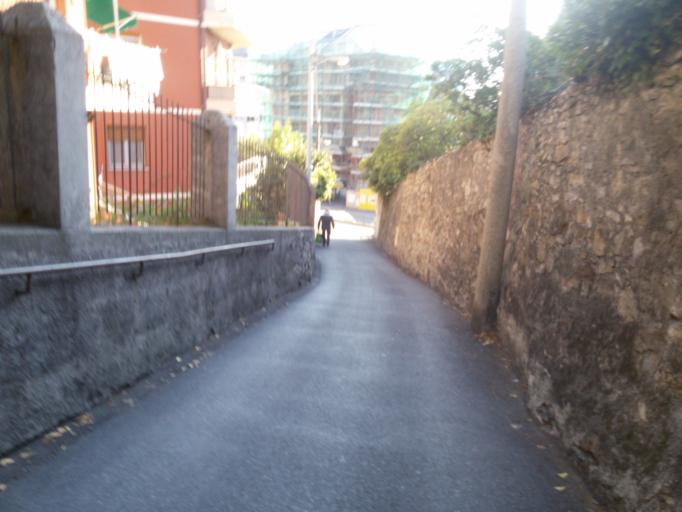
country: IT
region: Liguria
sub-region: Provincia di Genova
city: Genoa
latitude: 44.4088
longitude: 8.9774
